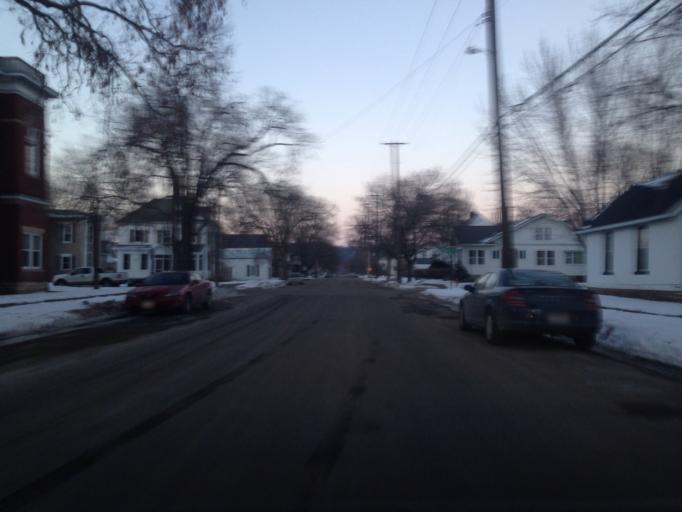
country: US
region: Minnesota
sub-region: Winona County
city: Winona
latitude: 44.0510
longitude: -91.6494
